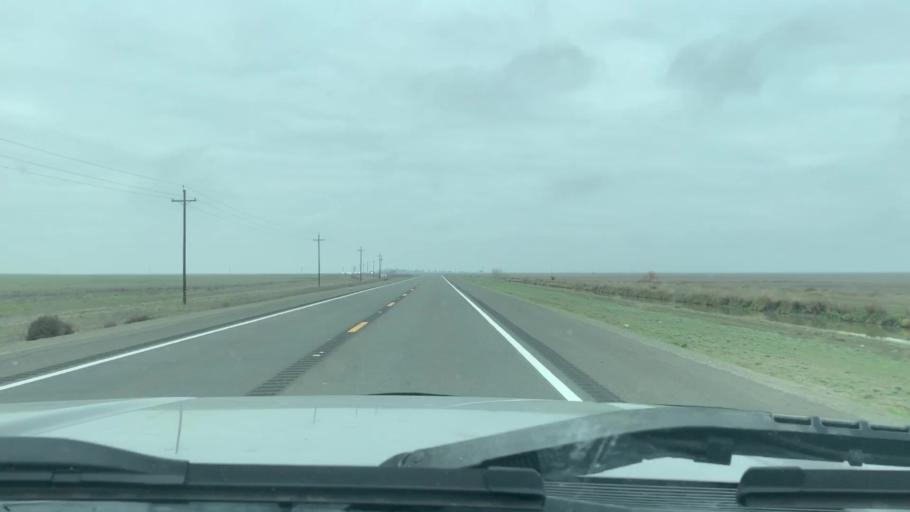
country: US
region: California
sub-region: Kings County
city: Kettleman City
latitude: 36.0851
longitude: -119.9167
